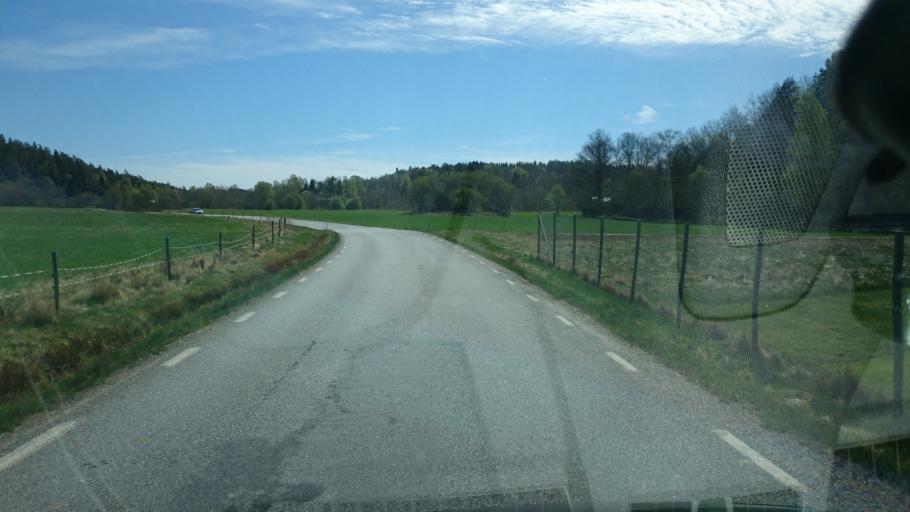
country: SE
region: Vaestra Goetaland
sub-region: Munkedals Kommun
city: Munkedal
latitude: 58.3768
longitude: 11.6790
